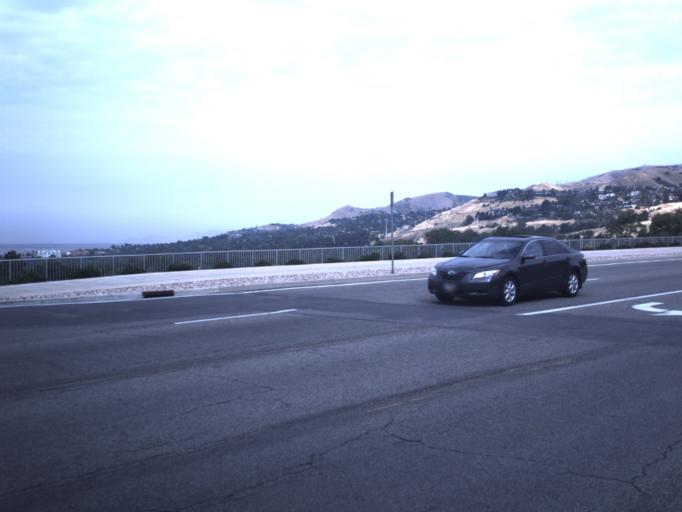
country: US
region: Utah
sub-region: Salt Lake County
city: Salt Lake City
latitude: 40.7716
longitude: -111.8404
